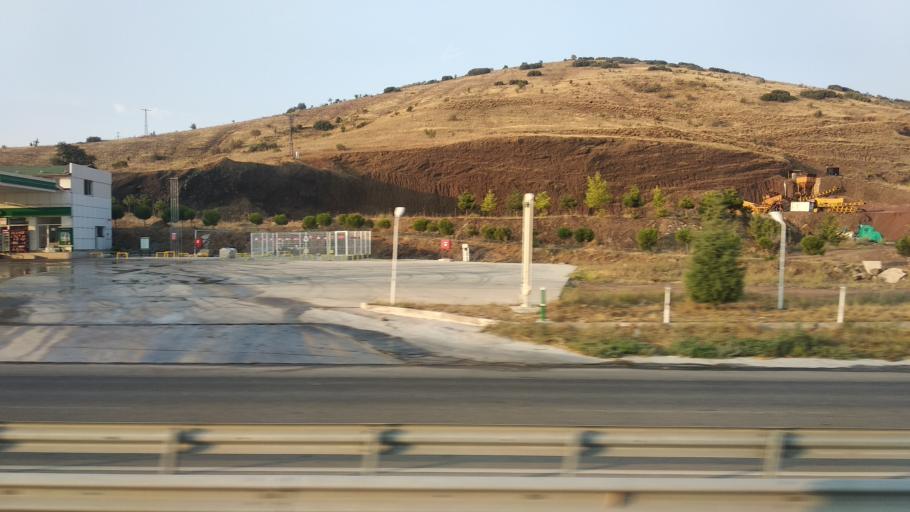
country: TR
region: Manisa
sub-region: Kula
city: Kula
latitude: 38.5669
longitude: 28.5820
